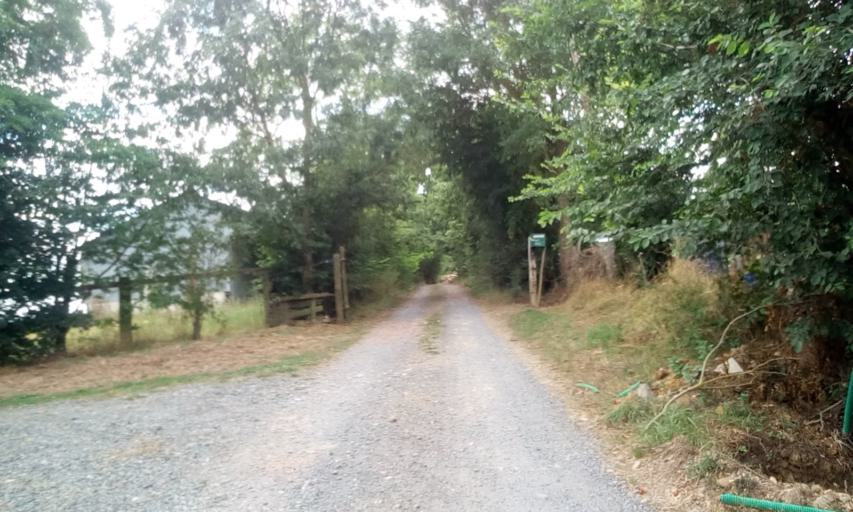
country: FR
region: Lower Normandy
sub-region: Departement du Calvados
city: Troarn
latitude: 49.1596
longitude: -0.1754
